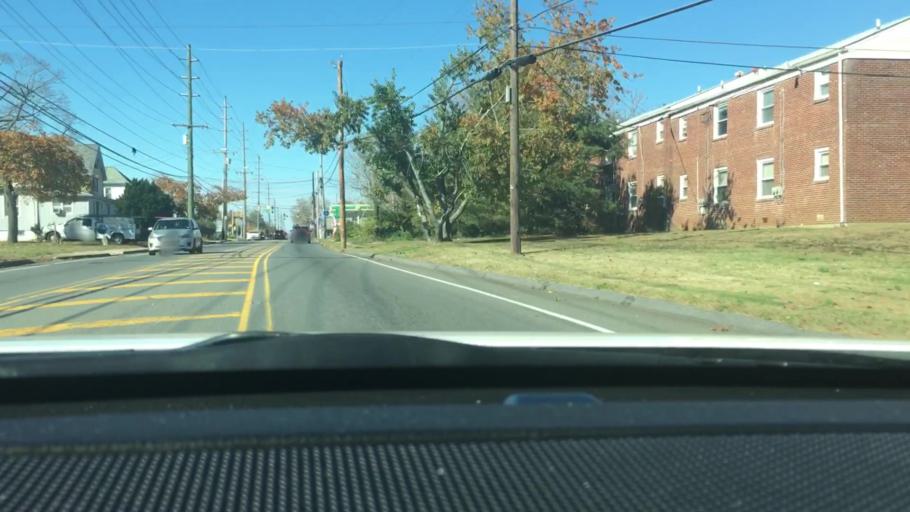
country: US
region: New Jersey
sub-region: Atlantic County
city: Pleasantville
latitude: 39.4034
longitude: -74.5095
